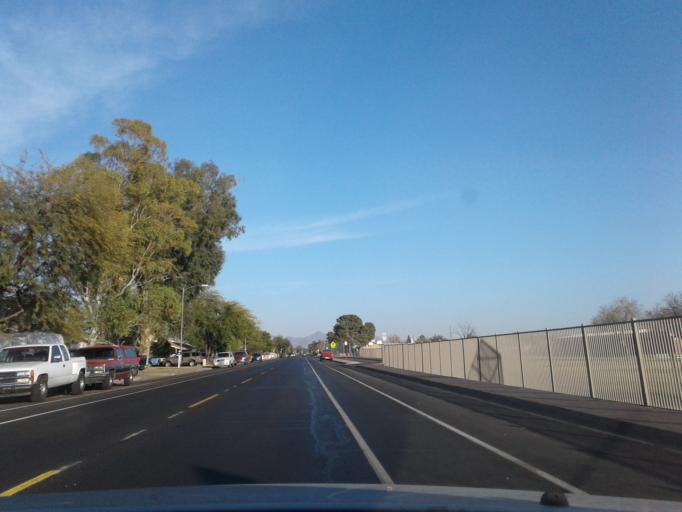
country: US
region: Arizona
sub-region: Maricopa County
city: Paradise Valley
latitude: 33.6478
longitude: -112.0266
